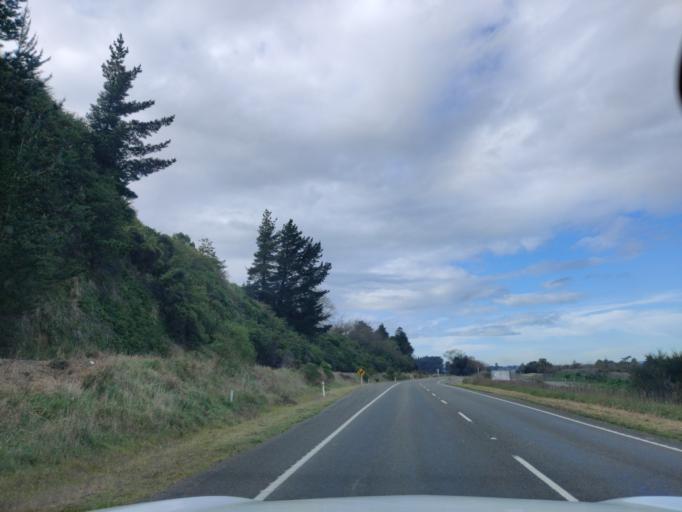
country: NZ
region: Manawatu-Wanganui
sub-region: Palmerston North City
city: Palmerston North
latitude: -40.3373
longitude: 175.8307
